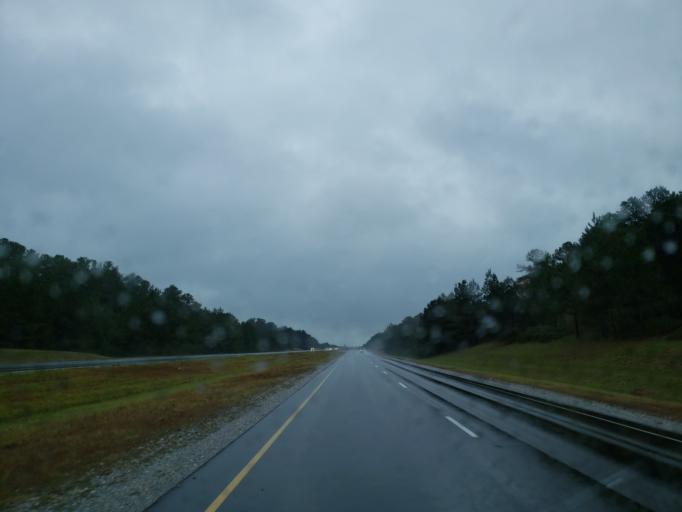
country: US
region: Mississippi
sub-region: Clarke County
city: Stonewall
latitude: 32.1337
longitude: -88.7139
